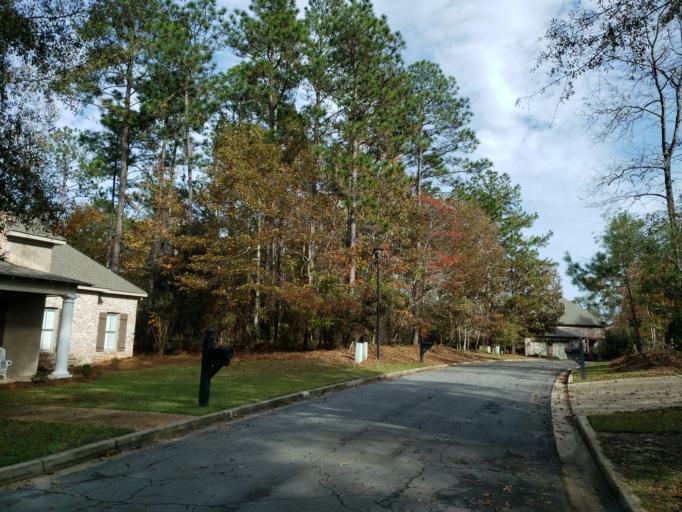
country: US
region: Mississippi
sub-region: Lamar County
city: West Hattiesburg
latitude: 31.3224
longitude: -89.4748
